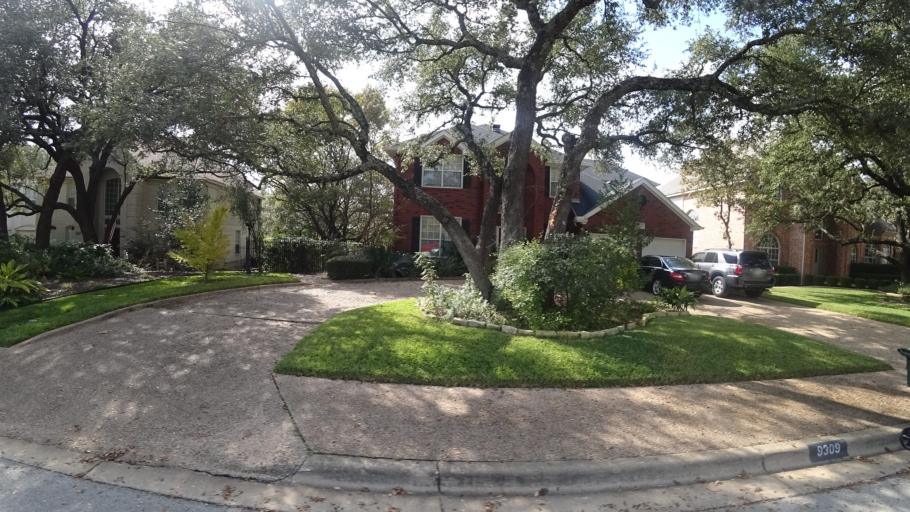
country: US
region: Texas
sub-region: Travis County
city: Barton Creek
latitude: 30.3003
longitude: -97.8833
